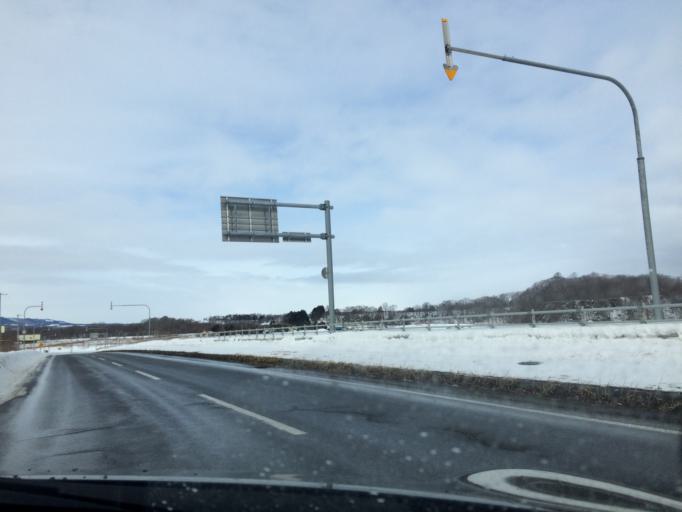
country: JP
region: Hokkaido
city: Iwamizawa
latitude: 42.9806
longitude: 141.8693
